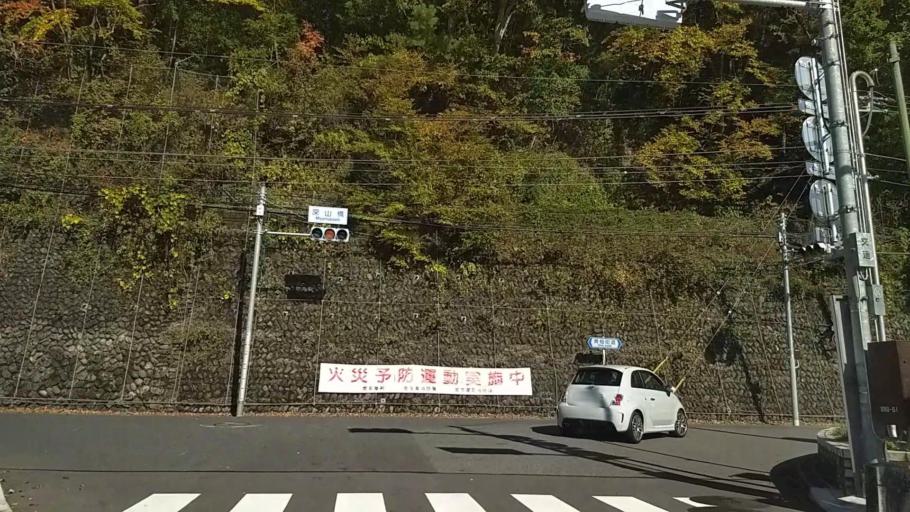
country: JP
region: Yamanashi
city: Otsuki
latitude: 35.7755
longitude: 139.0004
